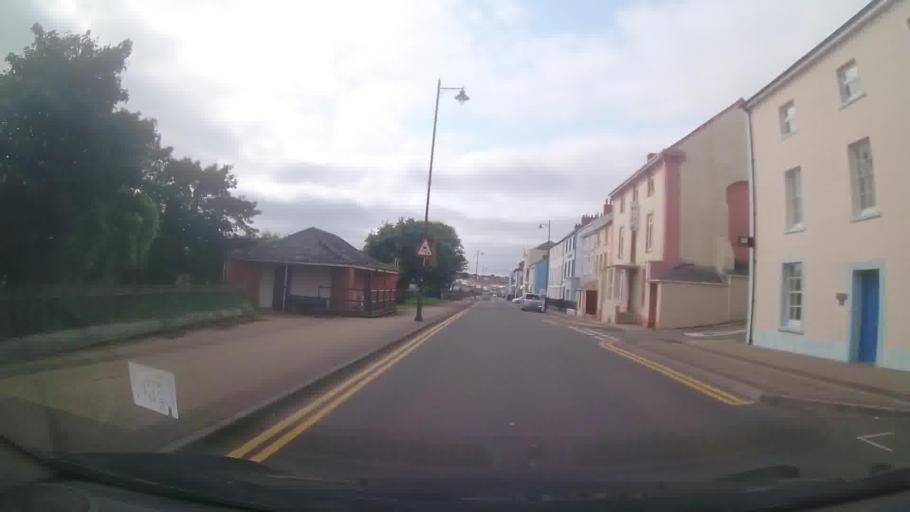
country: GB
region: Wales
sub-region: Pembrokeshire
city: Milford Haven
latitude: 51.7122
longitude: -5.0348
